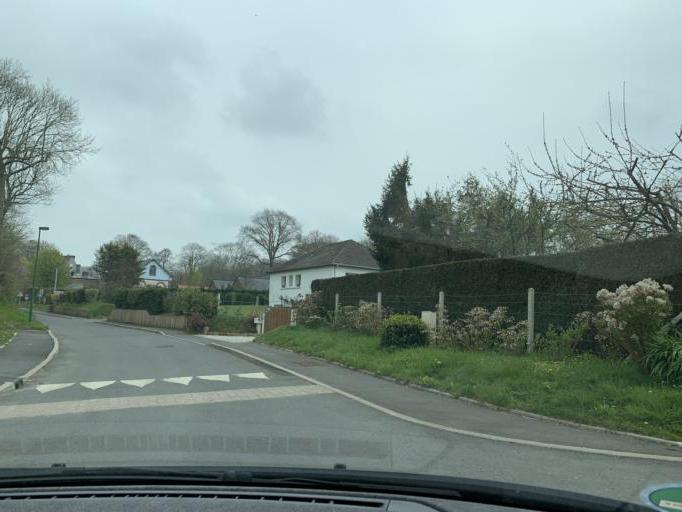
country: FR
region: Haute-Normandie
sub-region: Departement de la Seine-Maritime
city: Saint-Valery-en-Caux
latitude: 49.8540
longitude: 0.7904
